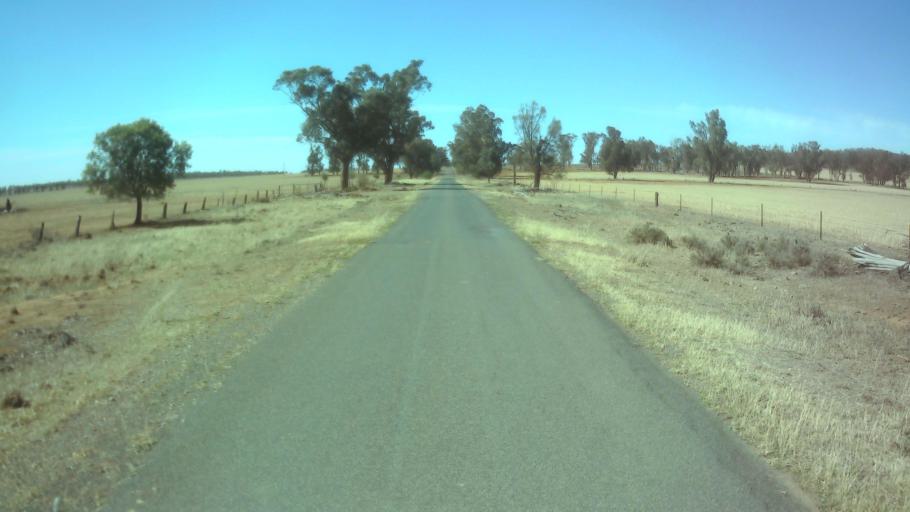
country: AU
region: New South Wales
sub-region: Forbes
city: Forbes
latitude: -33.7357
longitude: 147.7419
